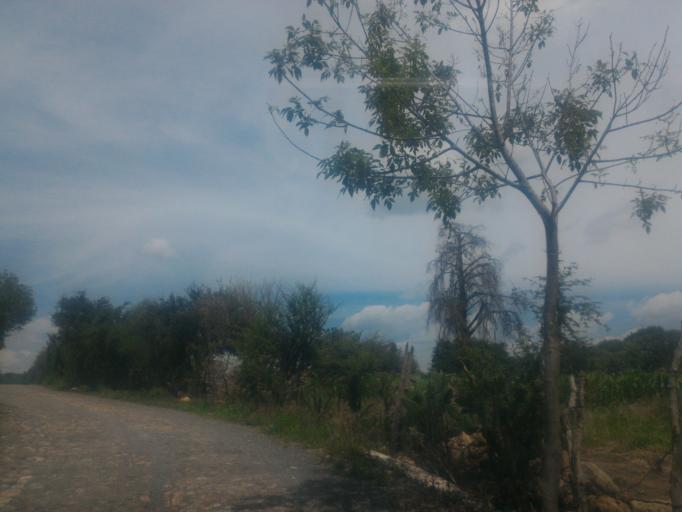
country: MX
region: Guanajuato
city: Ciudad Manuel Doblado
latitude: 20.7998
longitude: -102.0814
